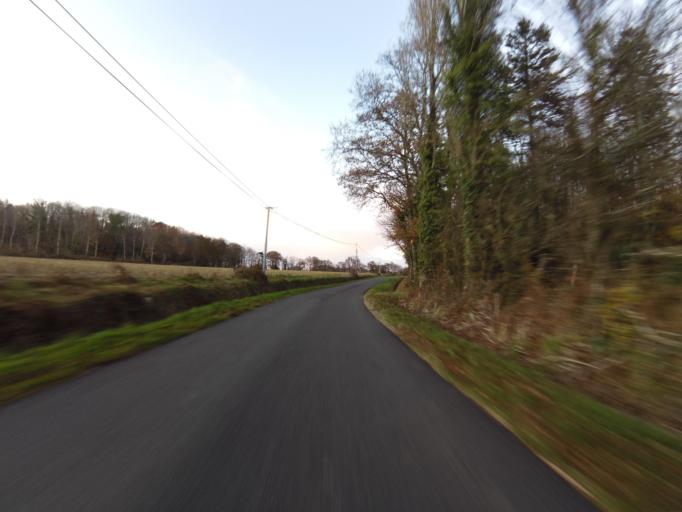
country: FR
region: Brittany
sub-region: Departement du Morbihan
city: Pluherlin
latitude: 47.7232
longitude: -2.3664
